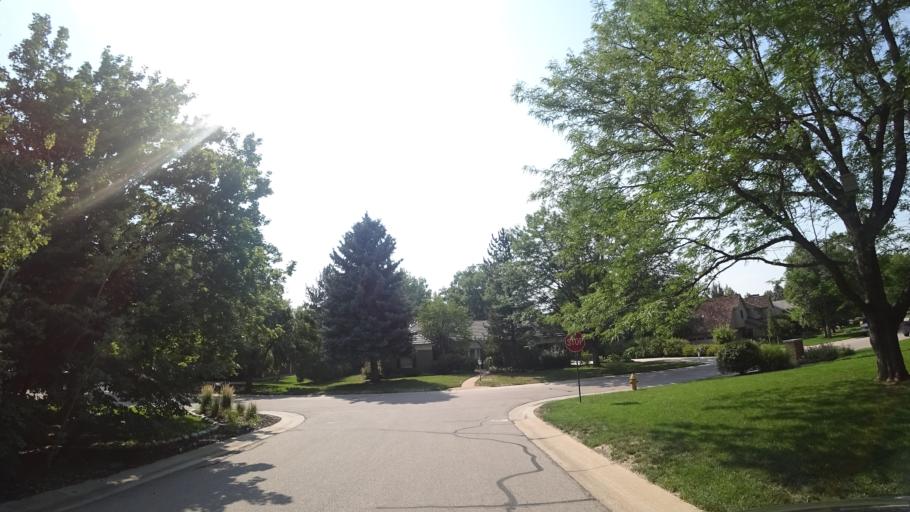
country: US
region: Colorado
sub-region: Arapahoe County
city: Greenwood Village
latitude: 39.6103
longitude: -104.9653
